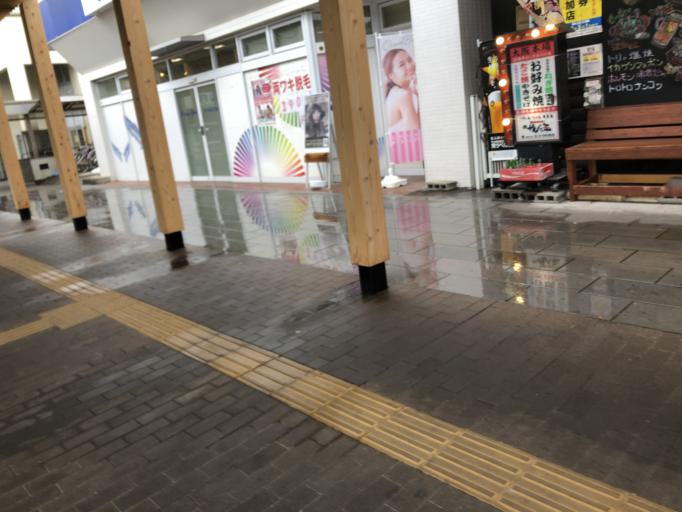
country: JP
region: Oita
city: Hita
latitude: 33.3171
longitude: 130.9384
